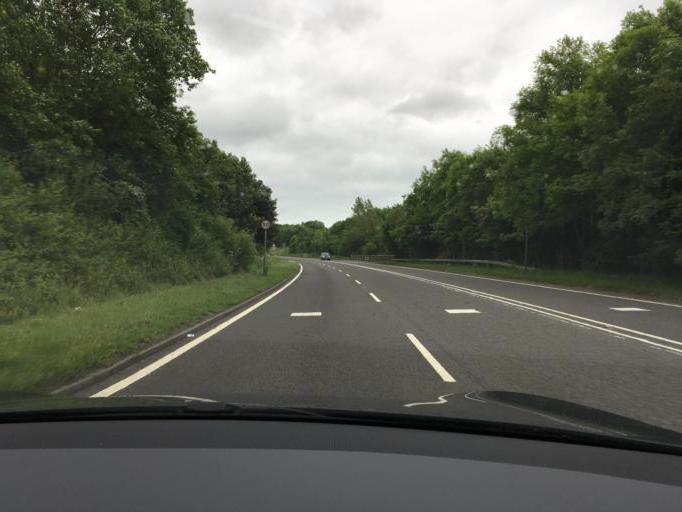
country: GB
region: England
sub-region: Derbyshire
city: Ashbourne
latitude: 53.0039
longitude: -1.7283
